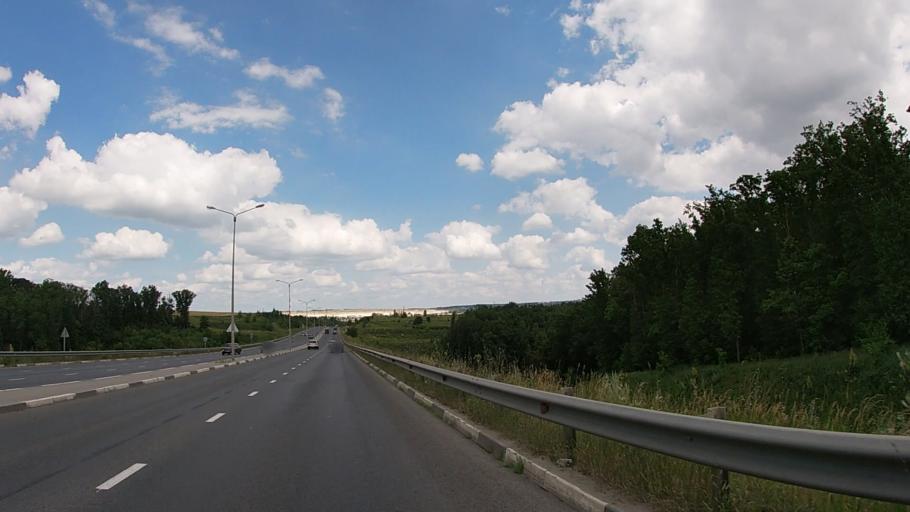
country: RU
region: Belgorod
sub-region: Belgorodskiy Rayon
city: Belgorod
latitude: 50.5990
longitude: 36.5303
